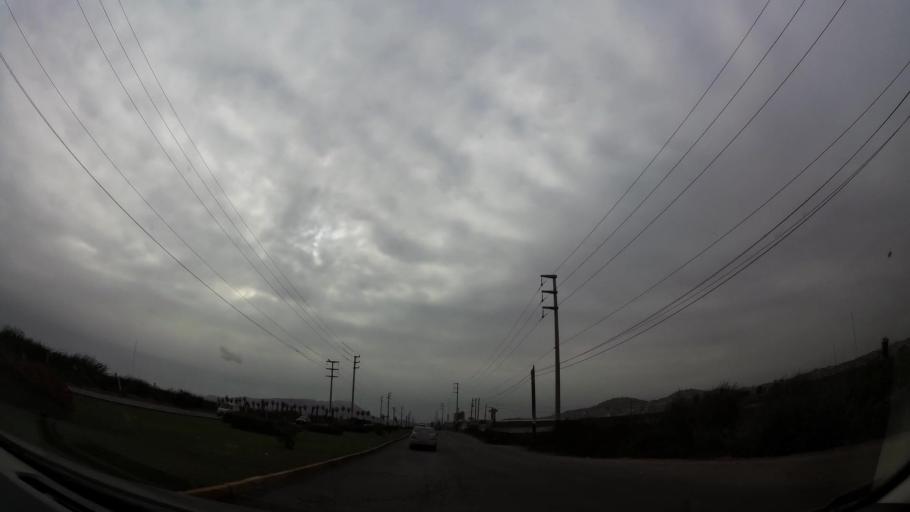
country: PE
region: Lima
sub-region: Lima
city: Surco
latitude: -12.2119
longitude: -76.9848
